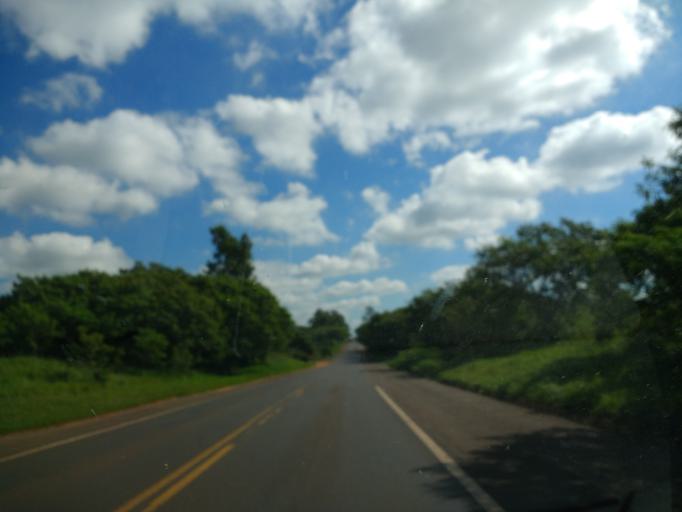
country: BR
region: Parana
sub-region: Alto Piquiri
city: Alto Piquiri
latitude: -23.8911
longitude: -53.4140
